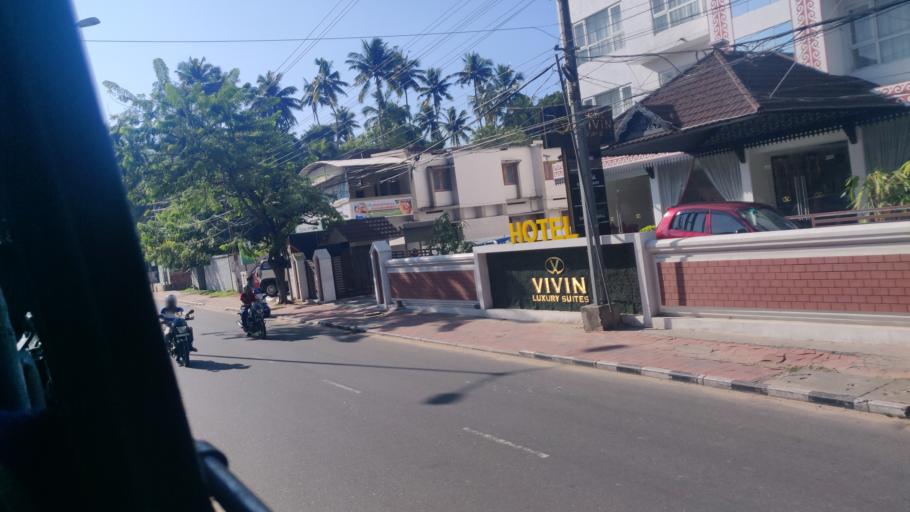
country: IN
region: Kerala
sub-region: Thiruvananthapuram
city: Thiruvananthapuram
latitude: 8.4973
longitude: 76.9360
